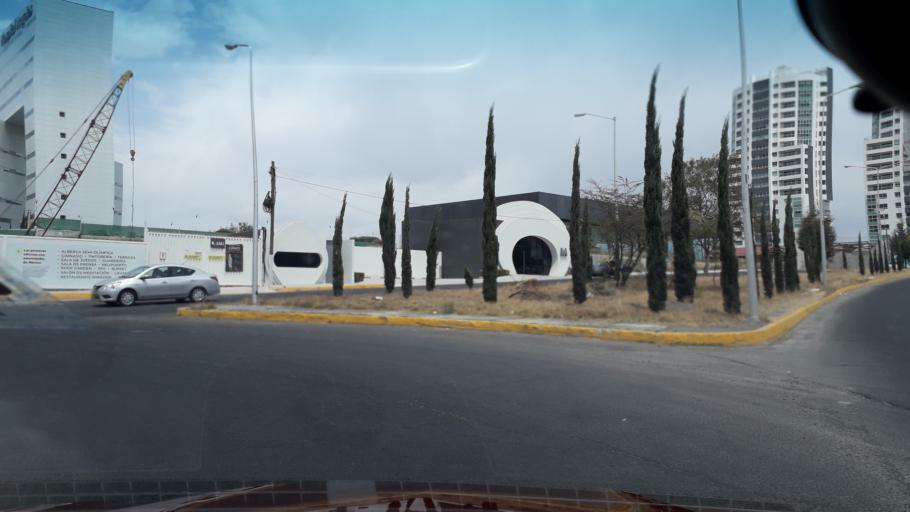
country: MX
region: Puebla
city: Puebla
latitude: 19.0196
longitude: -98.2360
